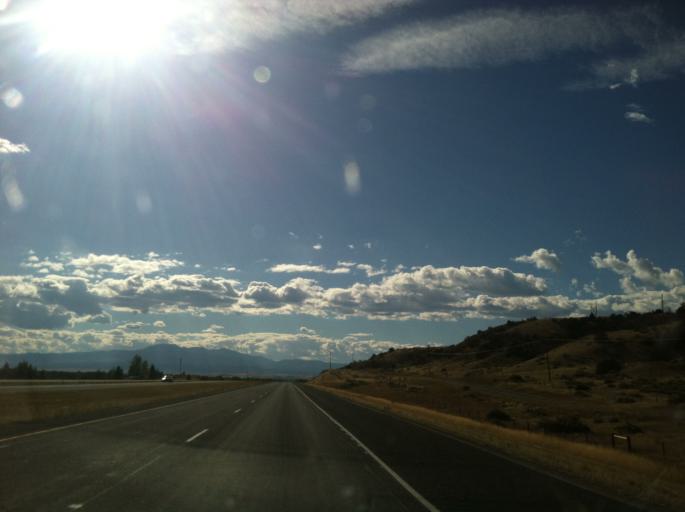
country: US
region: Montana
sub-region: Jefferson County
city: Whitehall
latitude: 45.8736
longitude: -112.0261
